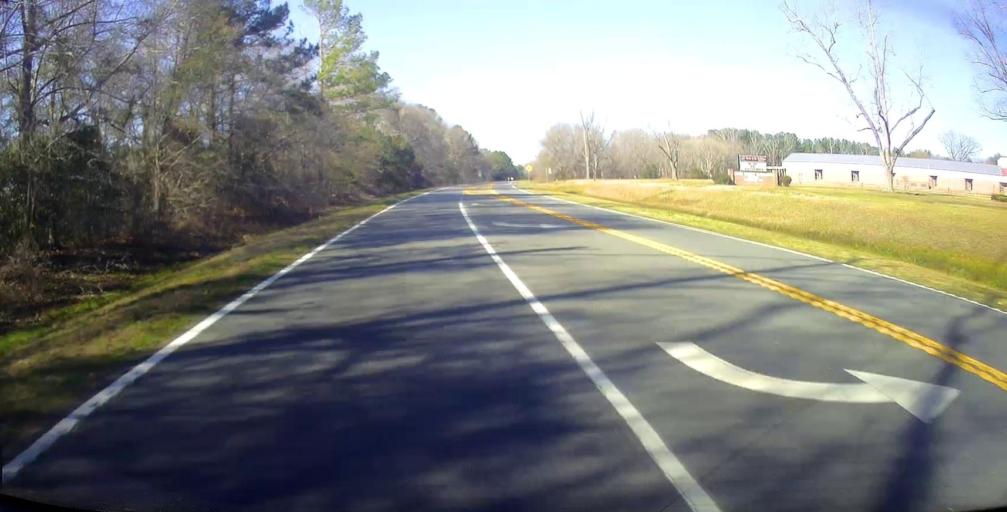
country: US
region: Georgia
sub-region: Macon County
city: Oglethorpe
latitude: 32.2877
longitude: -84.0750
